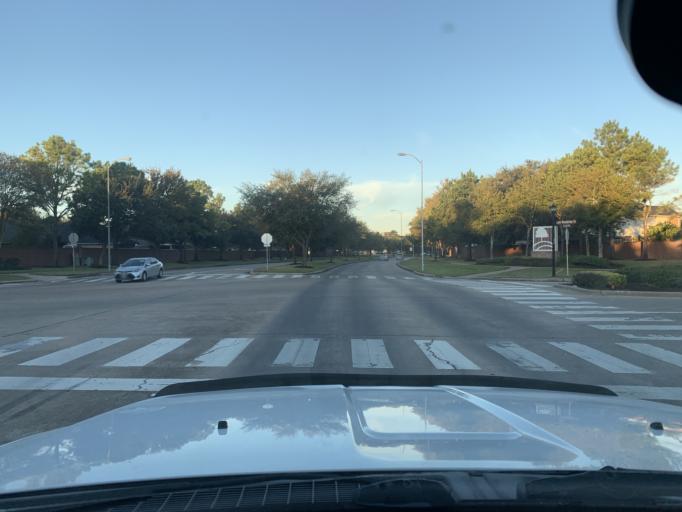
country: US
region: Texas
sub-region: Fort Bend County
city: Four Corners
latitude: 29.6482
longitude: -95.6447
